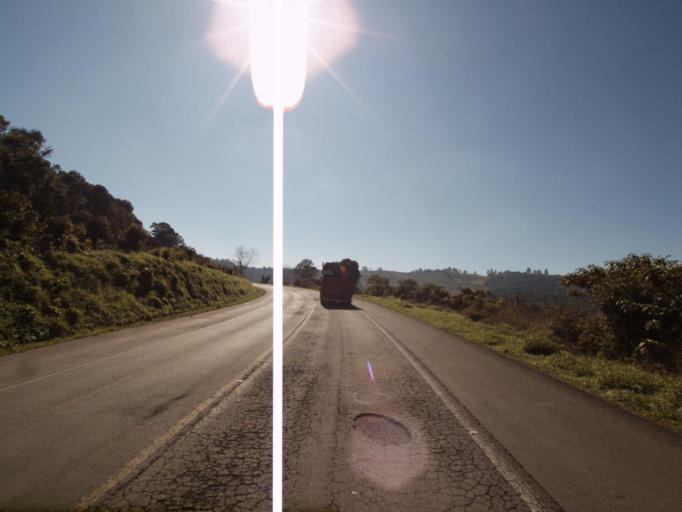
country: BR
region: Rio Grande do Sul
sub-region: Frederico Westphalen
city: Frederico Westphalen
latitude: -27.0650
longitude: -53.2216
